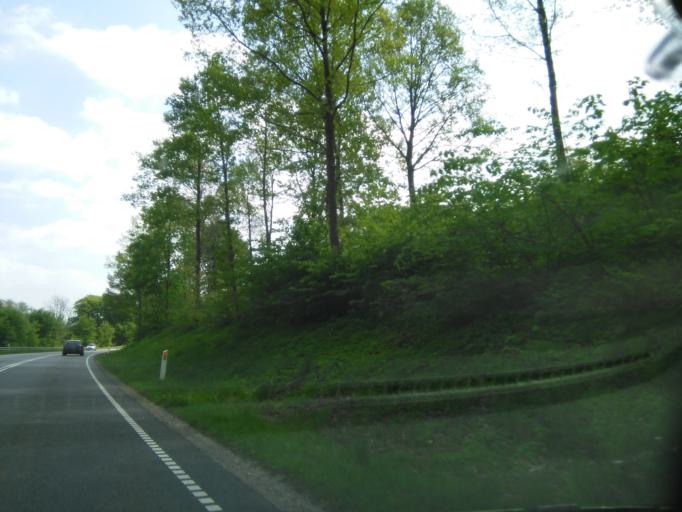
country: DK
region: Central Jutland
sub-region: Skanderborg Kommune
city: Skanderborg
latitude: 56.0284
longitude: 9.9624
